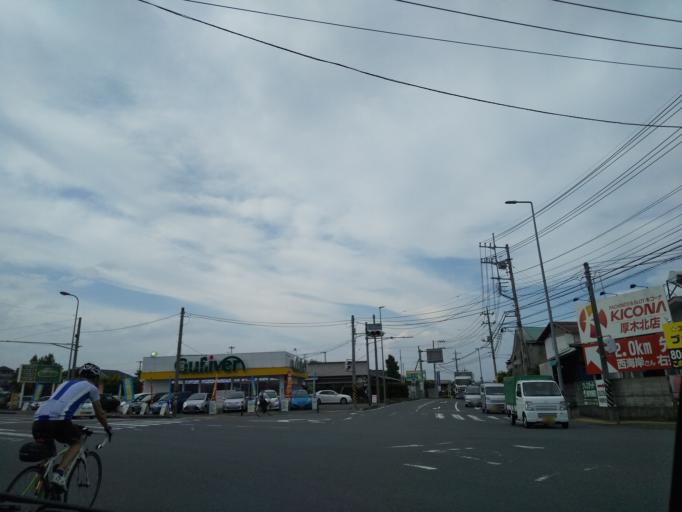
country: JP
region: Kanagawa
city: Atsugi
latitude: 35.4704
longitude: 139.3402
